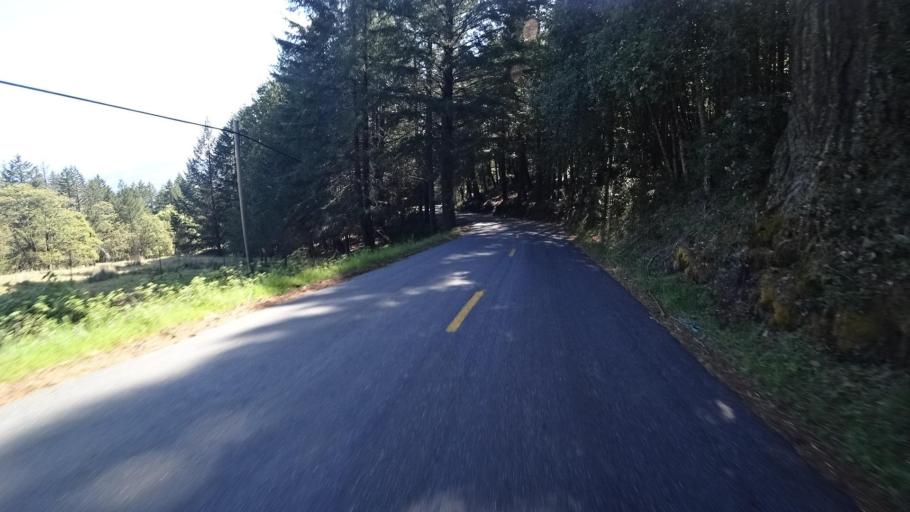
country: US
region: California
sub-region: Humboldt County
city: Redway
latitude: 40.0857
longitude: -123.6647
